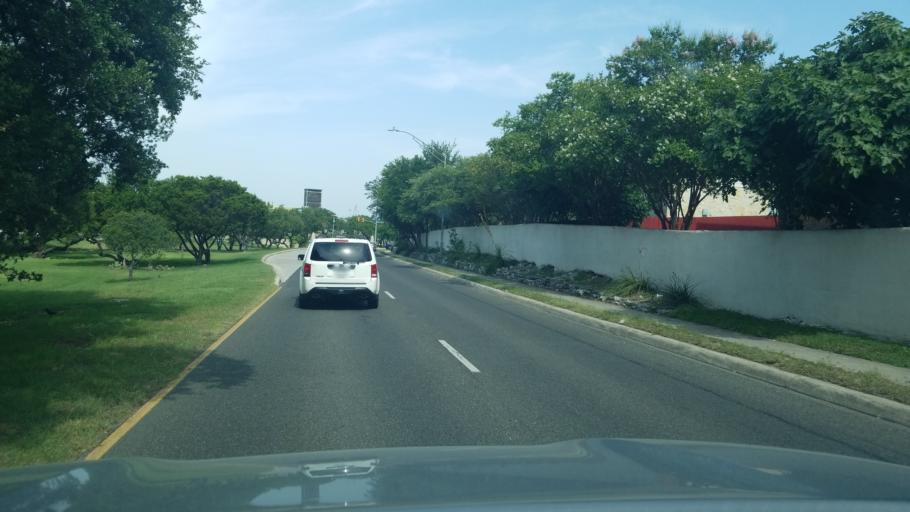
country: US
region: Texas
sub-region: Bexar County
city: Hollywood Park
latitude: 29.6387
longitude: -98.4606
